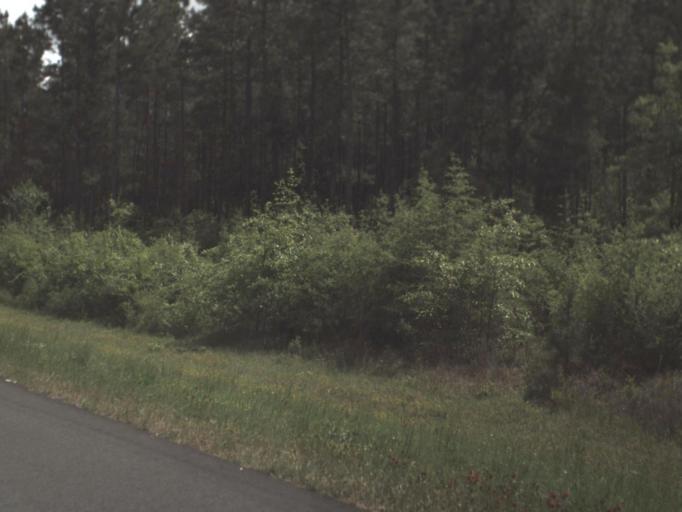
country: US
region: Florida
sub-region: Santa Rosa County
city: Wallace
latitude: 30.8430
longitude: -87.1453
